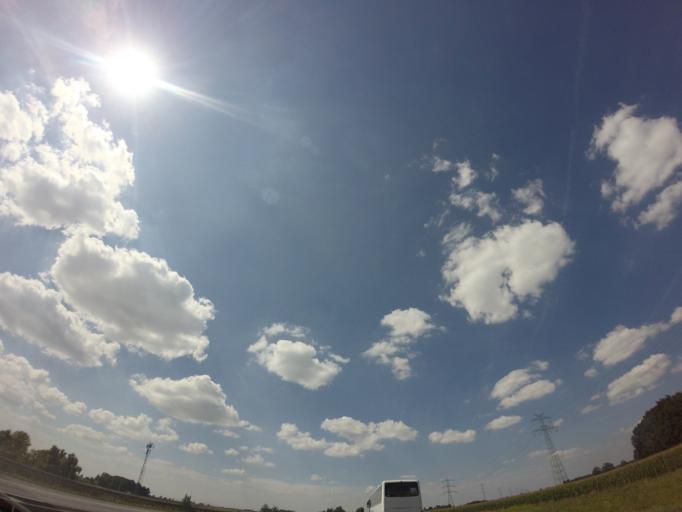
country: PL
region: Lower Silesian Voivodeship
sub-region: Powiat strzelinski
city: Wiazow
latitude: 50.8492
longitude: 17.2403
